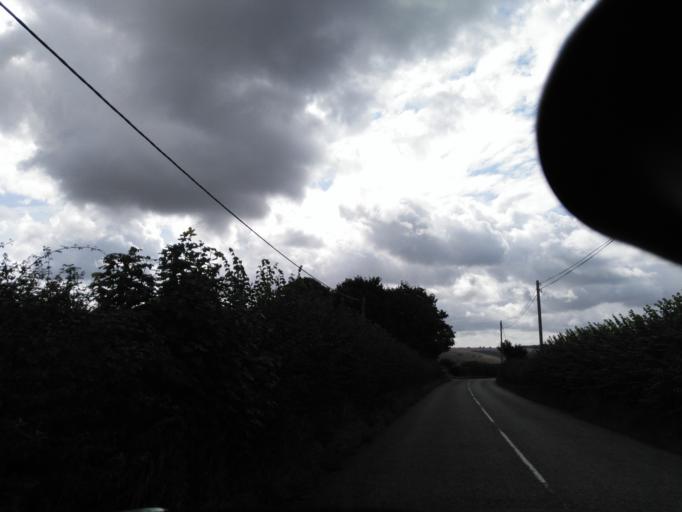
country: GB
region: England
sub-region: Dorset
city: Shaftesbury
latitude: 50.9939
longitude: -2.1733
